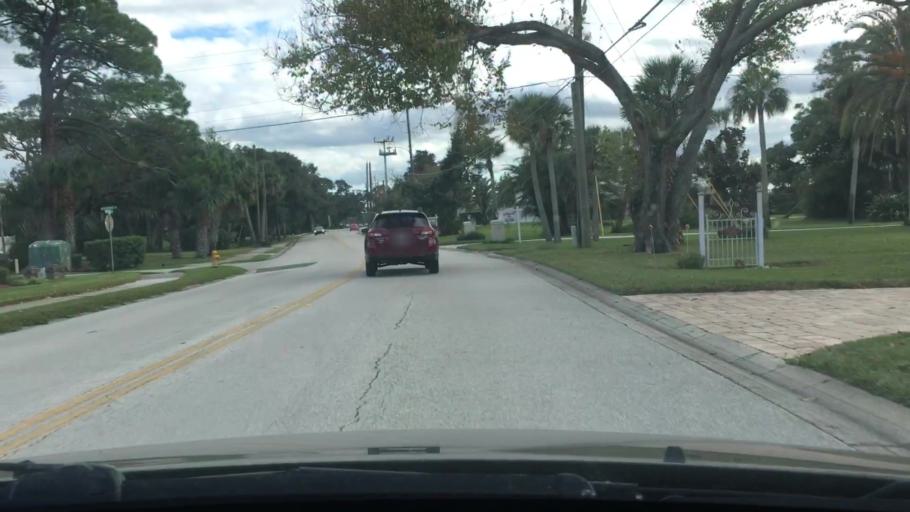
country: US
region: Florida
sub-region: Volusia County
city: Ormond Beach
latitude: 29.2740
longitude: -81.0402
